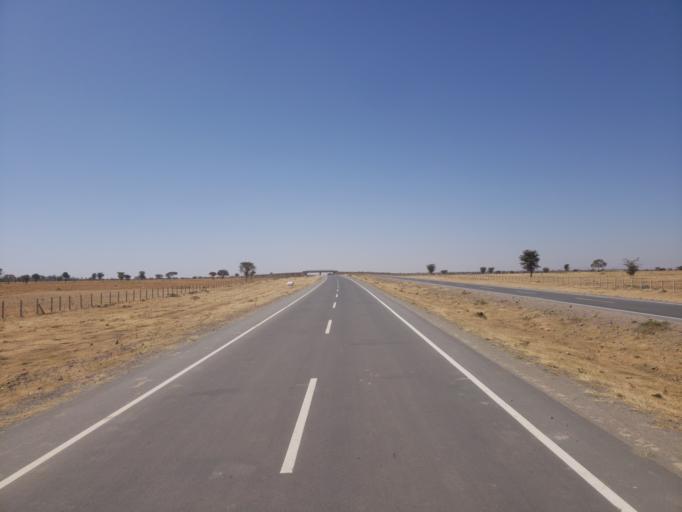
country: ET
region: Oromiya
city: Ziway
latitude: 8.2495
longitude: 38.8879
